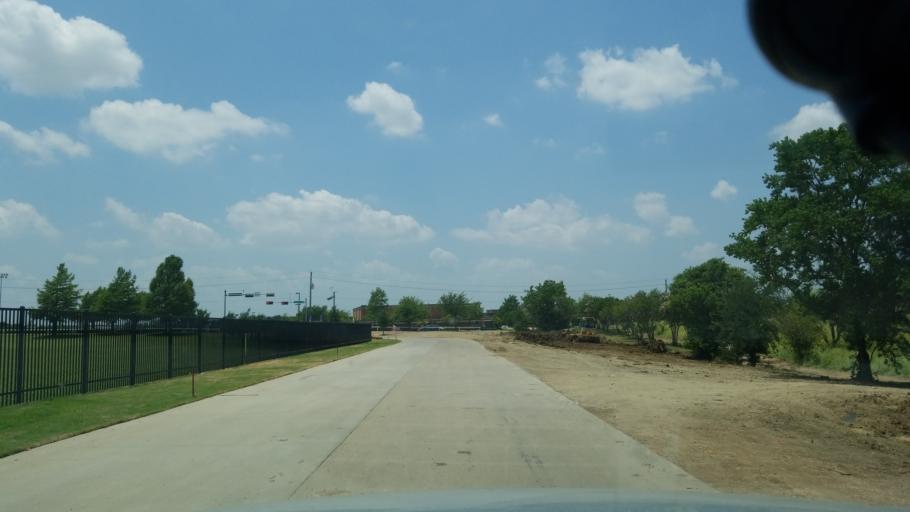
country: US
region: Texas
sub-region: Dallas County
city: Carrollton
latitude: 32.9648
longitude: -96.8764
